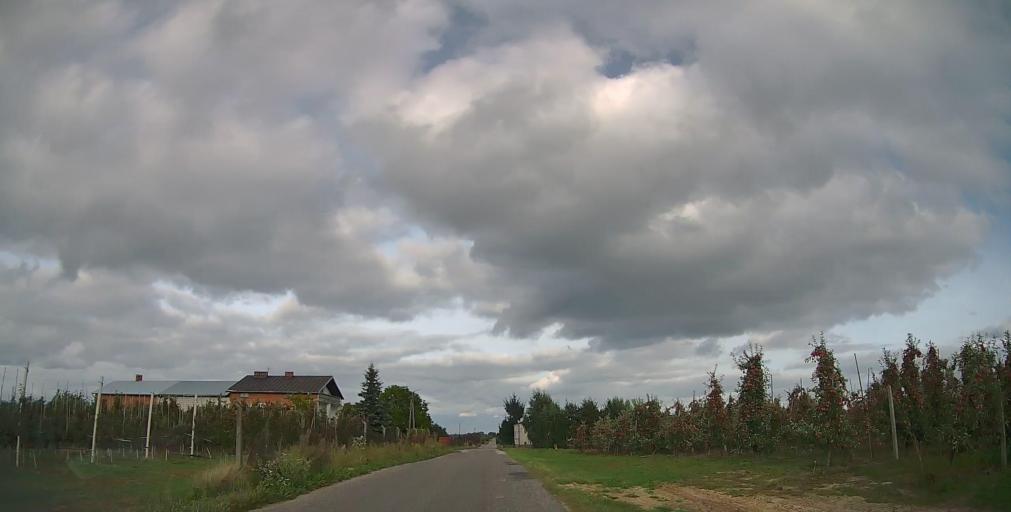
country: PL
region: Masovian Voivodeship
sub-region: Powiat grojecki
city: Jasieniec
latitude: 51.7685
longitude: 20.9046
